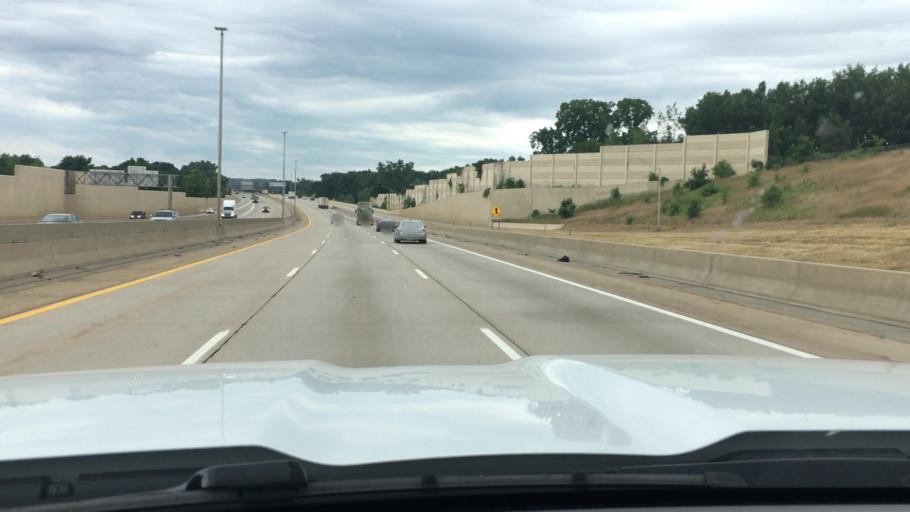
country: US
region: Michigan
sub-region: Kent County
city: Cutlerville
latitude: 42.8389
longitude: -85.6779
